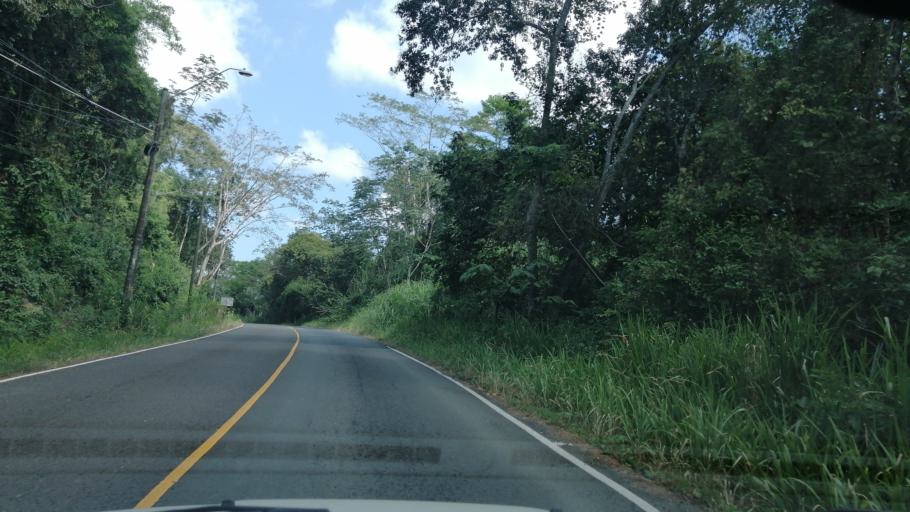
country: PA
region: Panama
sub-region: Distrito de Panama
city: Ancon
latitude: 8.9081
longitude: -79.5683
